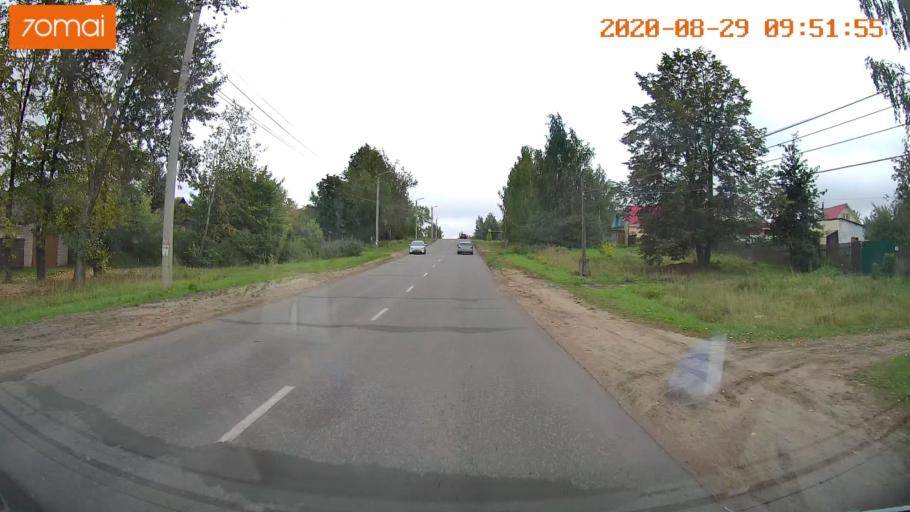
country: RU
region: Ivanovo
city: Kineshma
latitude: 57.4266
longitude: 42.2034
